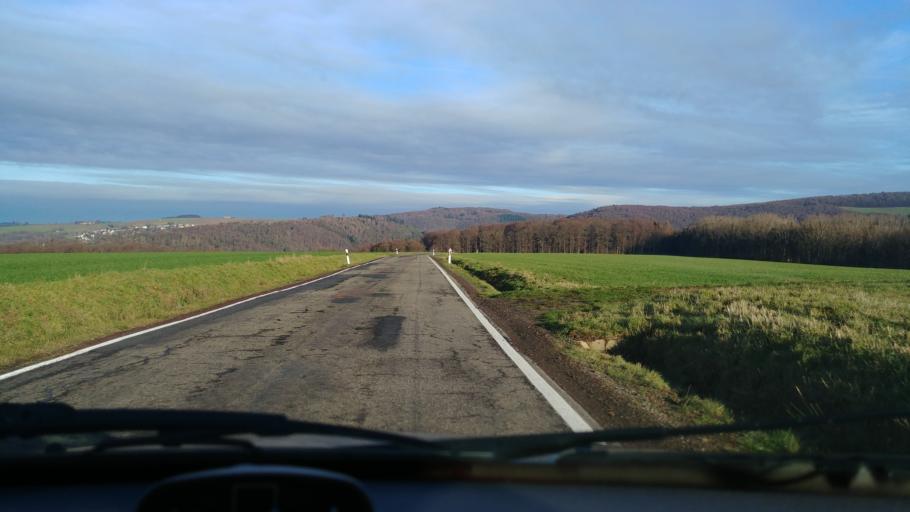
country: DE
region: Rheinland-Pfalz
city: Lollschied
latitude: 50.2720
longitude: 7.8566
